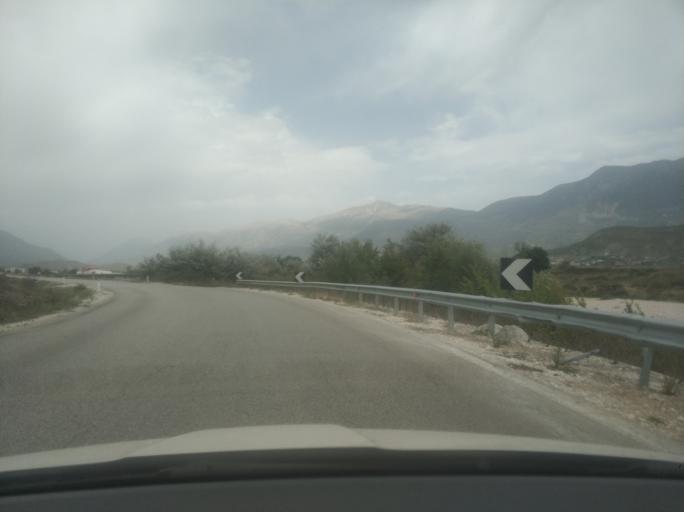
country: AL
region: Gjirokaster
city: Gjirokaster
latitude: 40.1082
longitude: 20.1225
